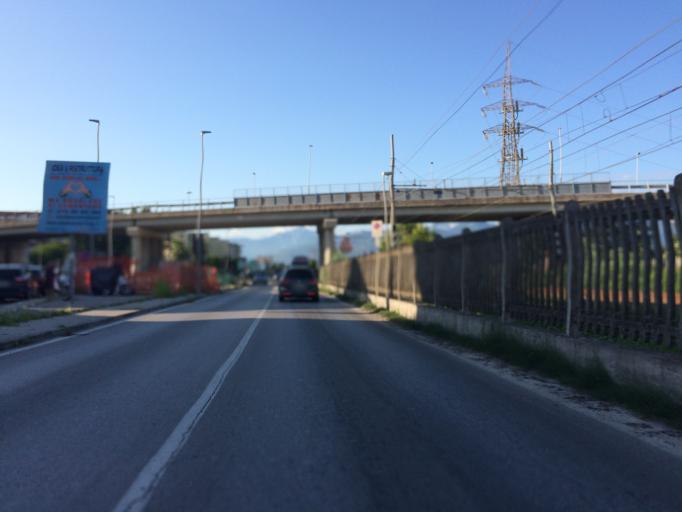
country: IT
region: Tuscany
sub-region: Provincia di Lucca
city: Viareggio
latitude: 43.8807
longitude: 10.2512
